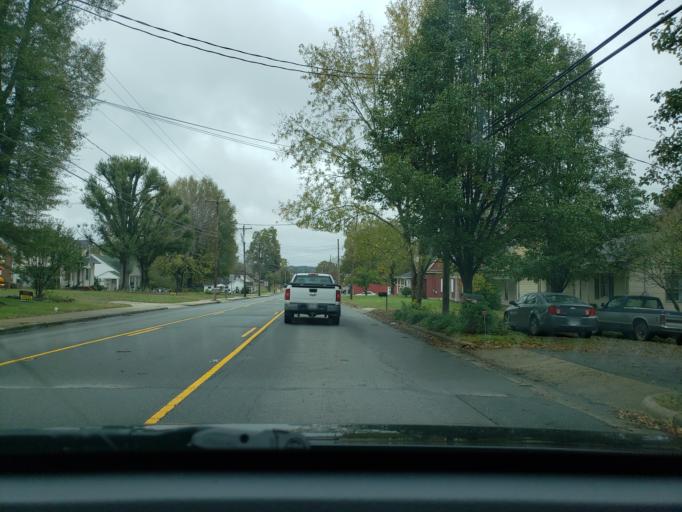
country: US
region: North Carolina
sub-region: Stokes County
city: Walnut Cove
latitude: 36.3038
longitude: -80.1414
